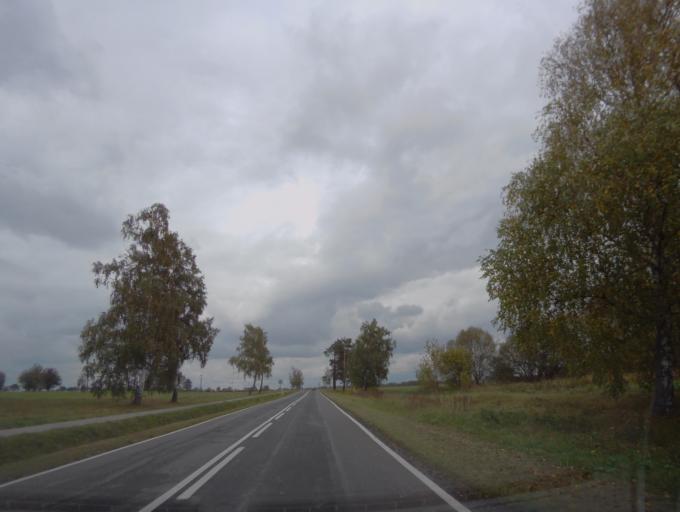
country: PL
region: Lublin Voivodeship
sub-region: Powiat wlodawski
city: Wlodawa
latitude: 51.6402
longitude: 23.5227
